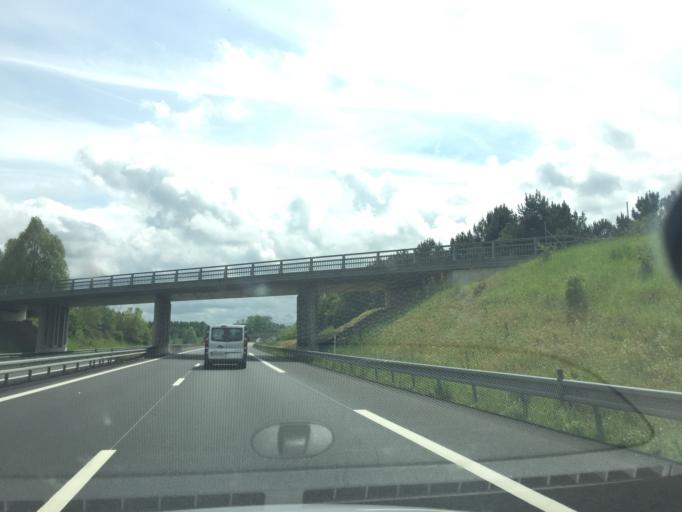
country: FR
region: Pays de la Loire
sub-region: Departement de la Sarthe
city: Marigne-Laille
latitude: 47.8148
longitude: 0.3073
